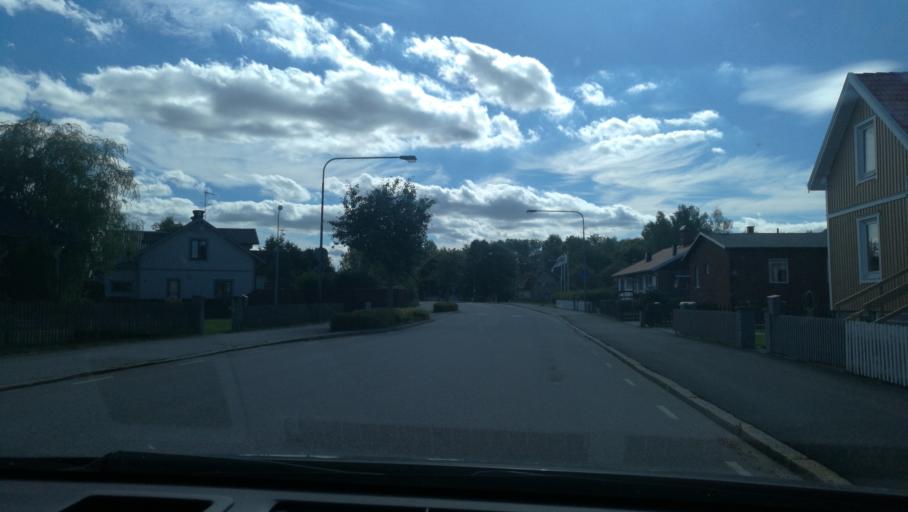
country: SE
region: Vaestra Goetaland
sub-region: Mariestads Kommun
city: Mariestad
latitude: 58.7002
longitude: 13.8367
